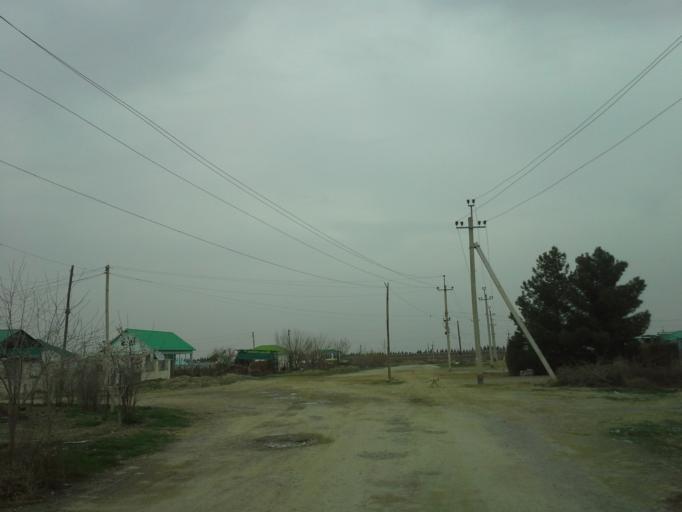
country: TM
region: Ahal
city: Abadan
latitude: 37.9760
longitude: 58.2258
